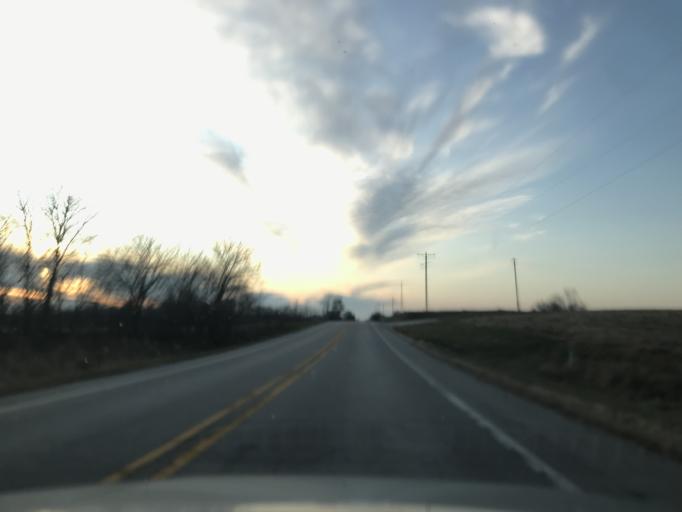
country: US
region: Illinois
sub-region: Henderson County
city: Oquawka
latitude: 41.0189
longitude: -90.8335
